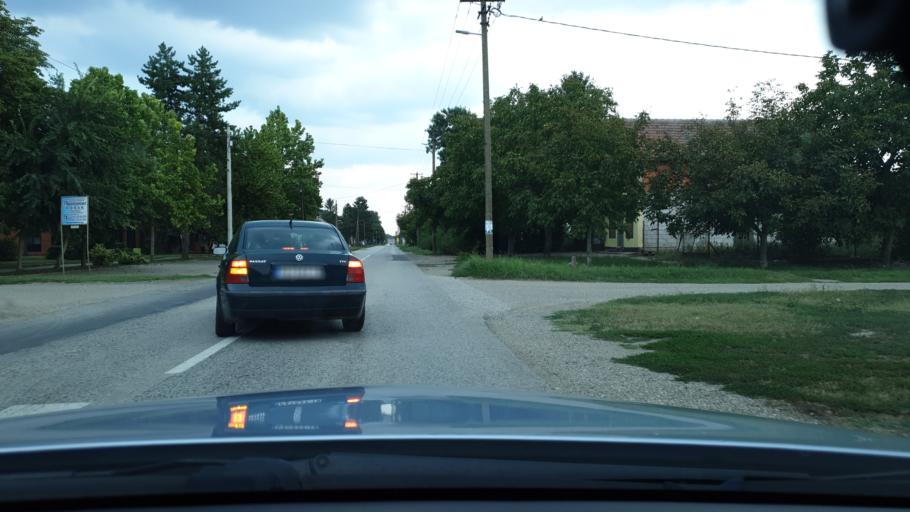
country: RS
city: Konak
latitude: 45.3140
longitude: 20.9090
